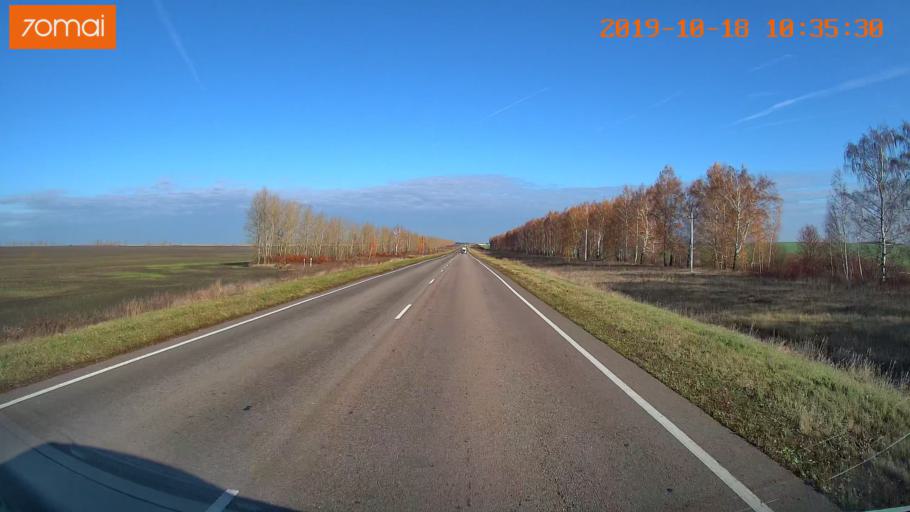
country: RU
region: Tula
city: Kurkino
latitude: 53.5341
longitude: 38.6203
